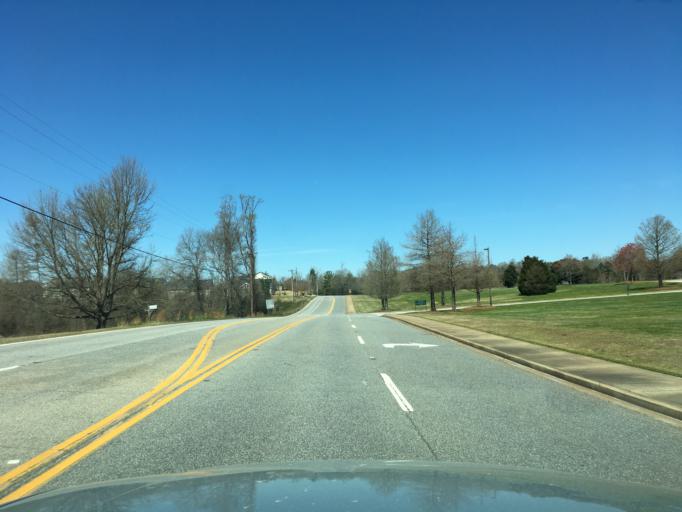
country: US
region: South Carolina
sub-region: Spartanburg County
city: Roebuck
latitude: 34.8818
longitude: -82.0047
